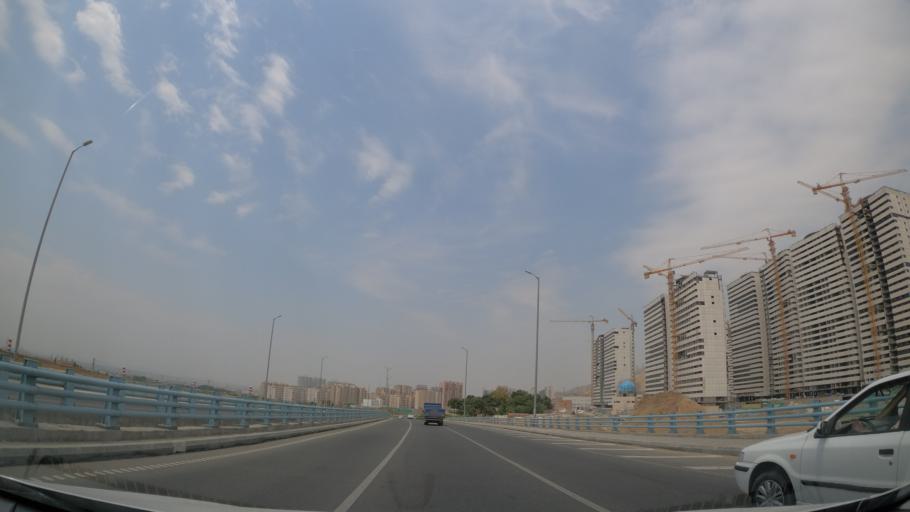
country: IR
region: Tehran
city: Shahr-e Qods
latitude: 35.7517
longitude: 51.1654
